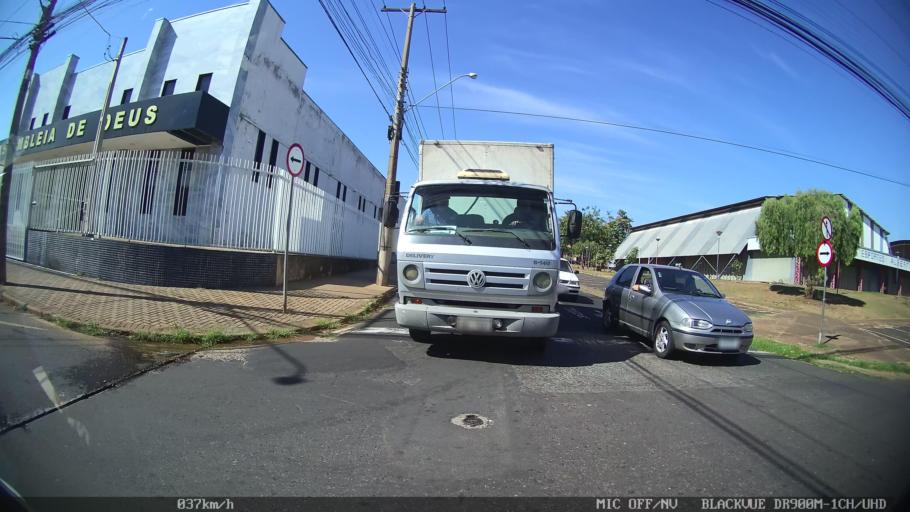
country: BR
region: Sao Paulo
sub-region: Sao Jose Do Rio Preto
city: Sao Jose do Rio Preto
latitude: -20.8052
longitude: -49.4012
